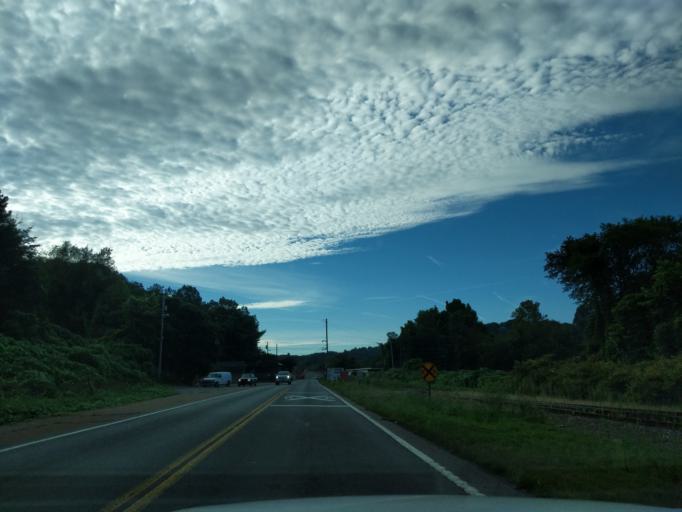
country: US
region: Georgia
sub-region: Fannin County
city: McCaysville
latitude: 34.9914
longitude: -84.3754
